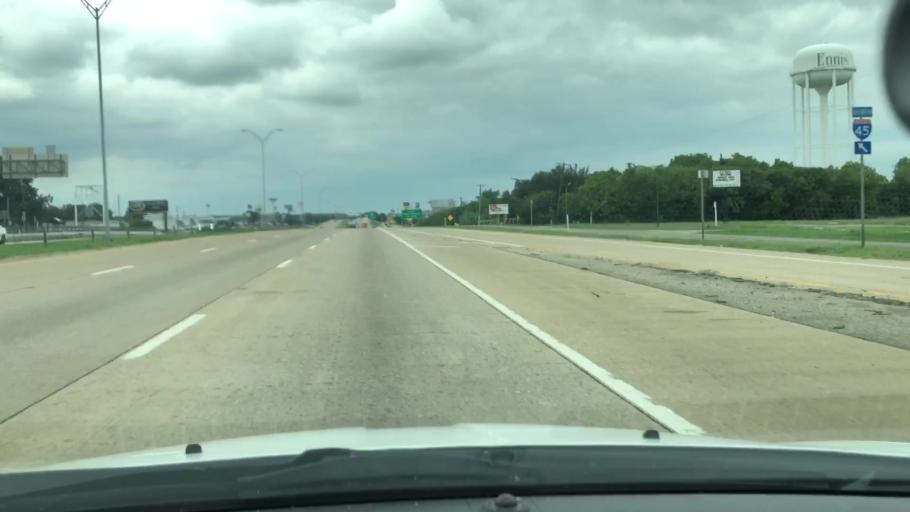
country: US
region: Texas
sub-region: Ellis County
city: Ennis
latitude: 32.3271
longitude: -96.6104
